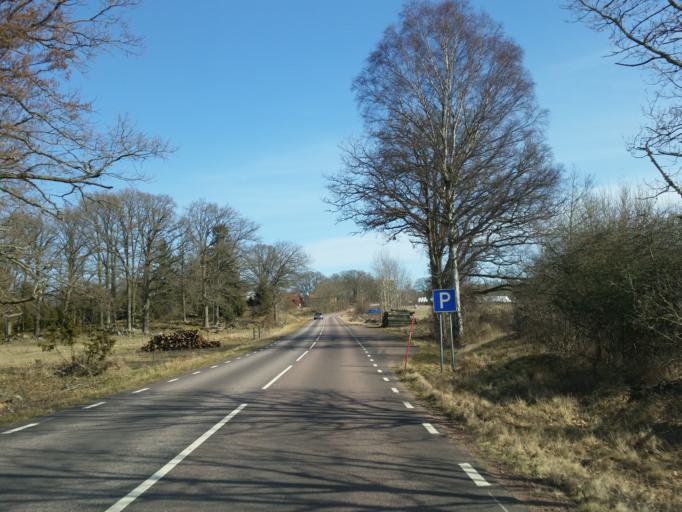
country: SE
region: Kalmar
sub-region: Monsteras Kommun
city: Timmernabben
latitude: 56.8637
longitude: 16.4105
